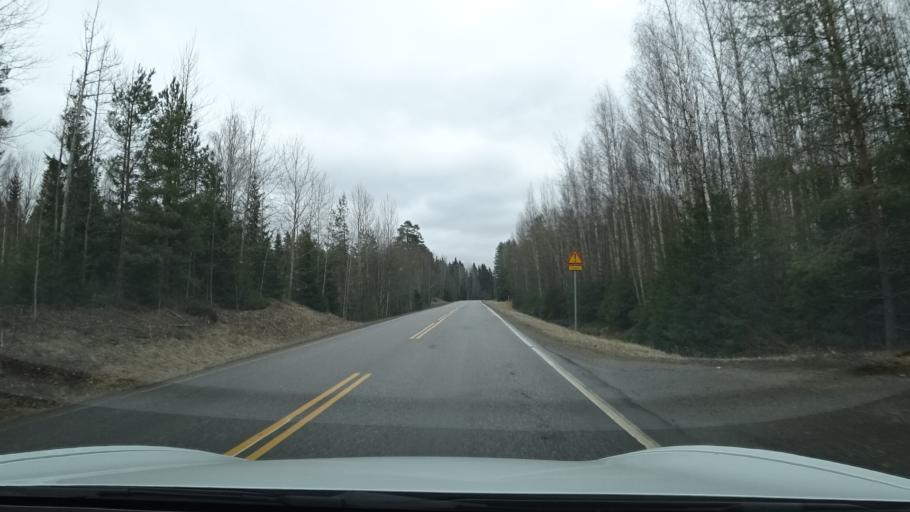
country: FI
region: Uusimaa
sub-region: Helsinki
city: Pornainen
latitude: 60.4859
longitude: 25.4119
